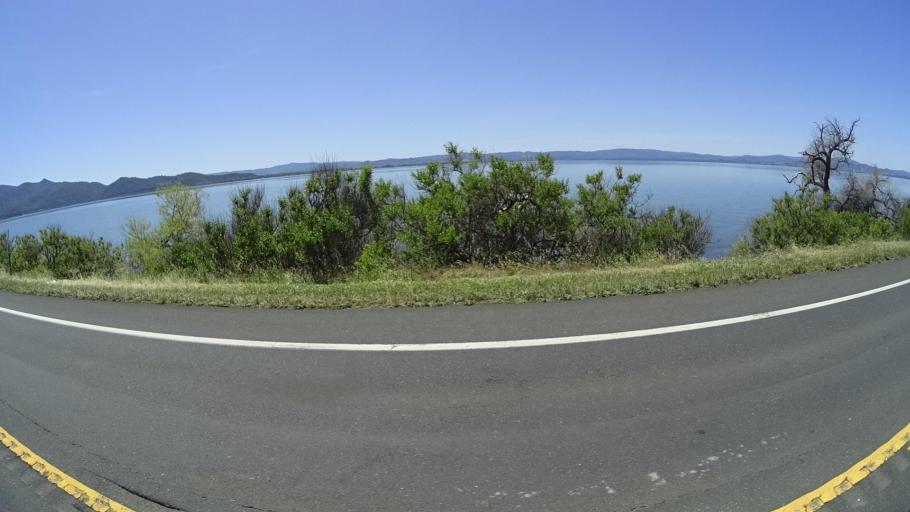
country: US
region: California
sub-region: Lake County
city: Lucerne
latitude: 39.0494
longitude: -122.7790
